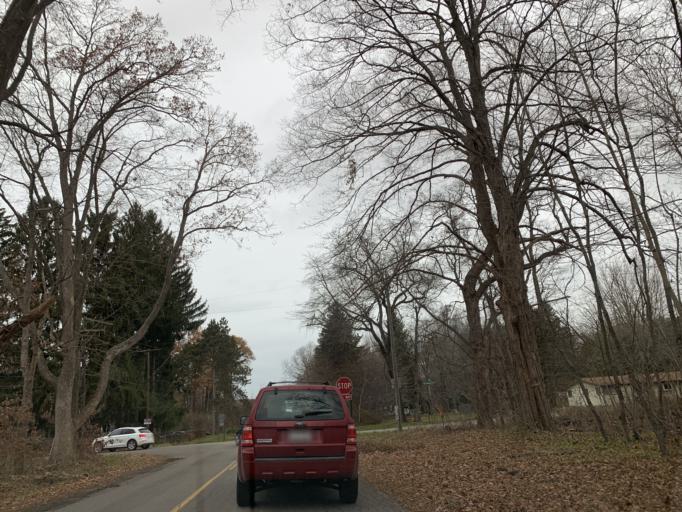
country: US
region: Michigan
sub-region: Berrien County
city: Three Oaks
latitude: 41.8276
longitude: -86.6683
